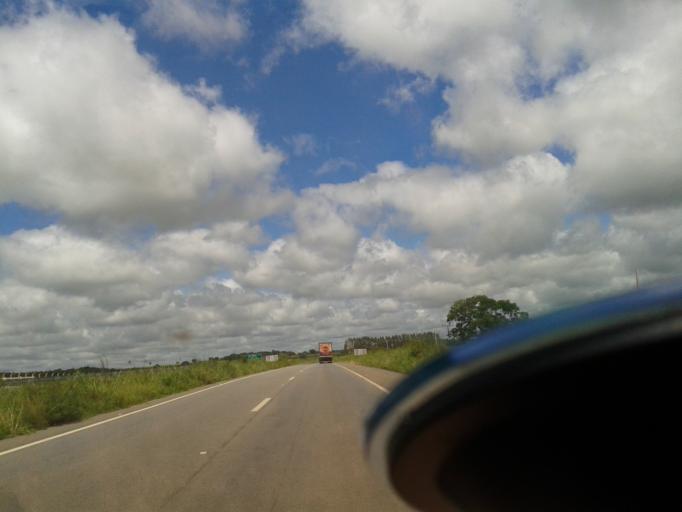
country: BR
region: Goias
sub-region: Itaberai
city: Itaberai
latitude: -16.1016
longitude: -49.6955
